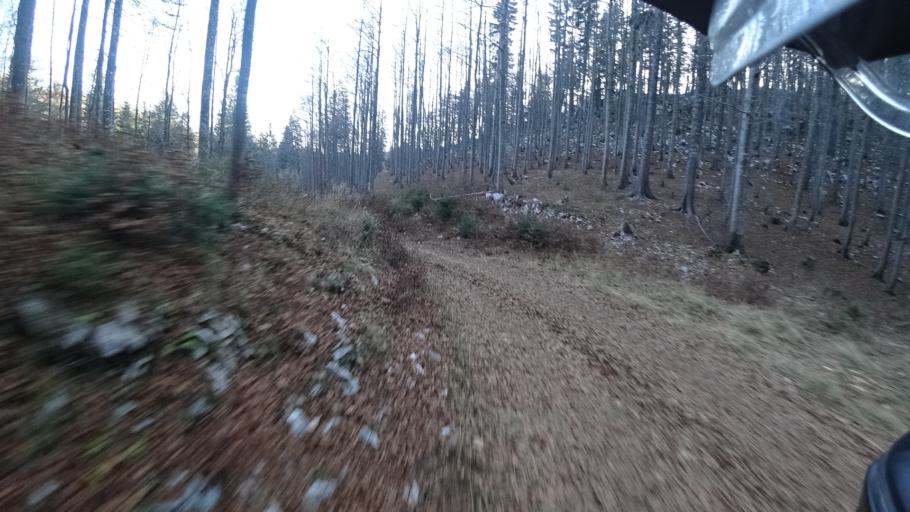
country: HR
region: Primorsko-Goranska
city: Drazice
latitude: 45.5023
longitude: 14.4819
